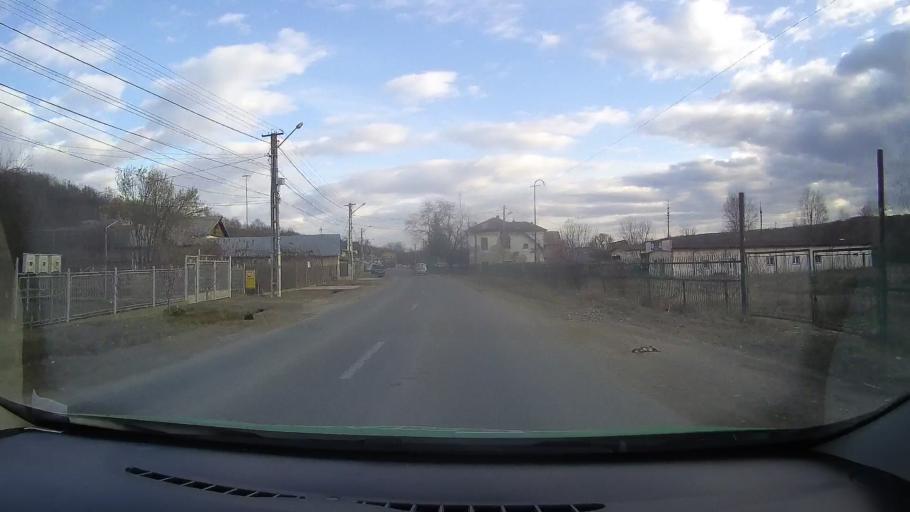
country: RO
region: Dambovita
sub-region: Comuna Gura Ocnitei
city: Gura Ocnitei
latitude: 44.9526
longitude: 25.5550
